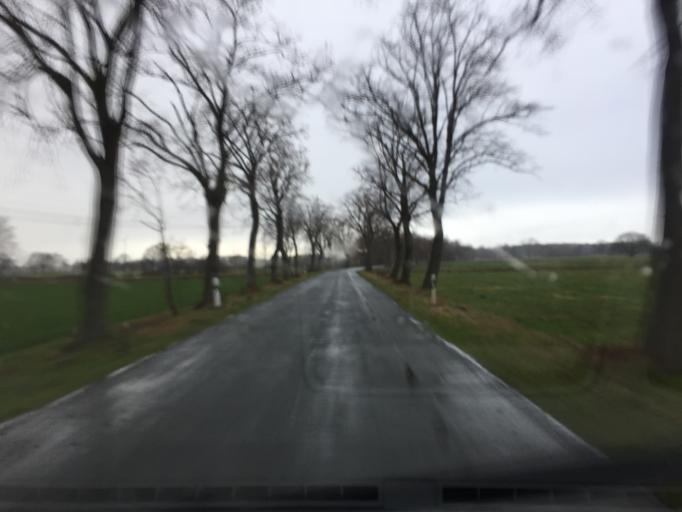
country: DE
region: Lower Saxony
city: Barenburg
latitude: 52.6472
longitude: 8.8228
